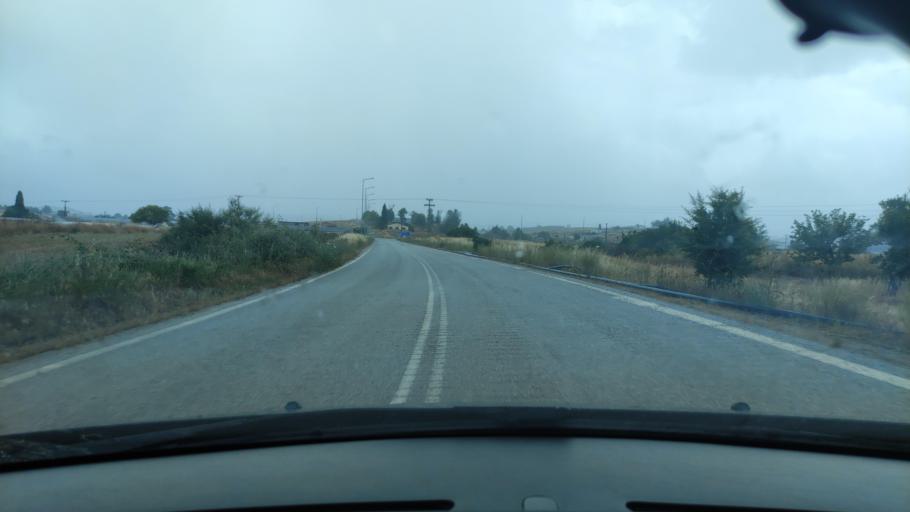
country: GR
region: Central Greece
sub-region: Nomos Evvoias
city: Afration
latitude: 38.5204
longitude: 23.7246
